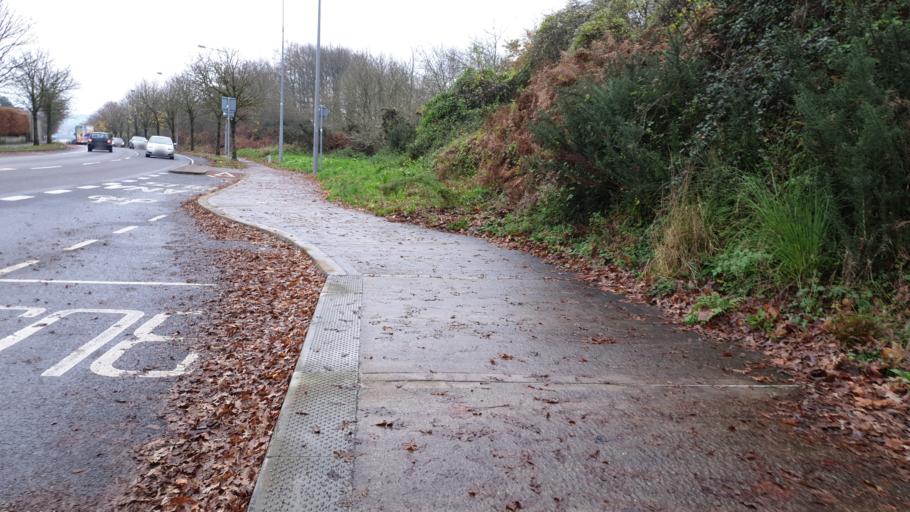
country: IE
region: Munster
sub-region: County Cork
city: Cork
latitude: 51.8894
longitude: -8.4102
